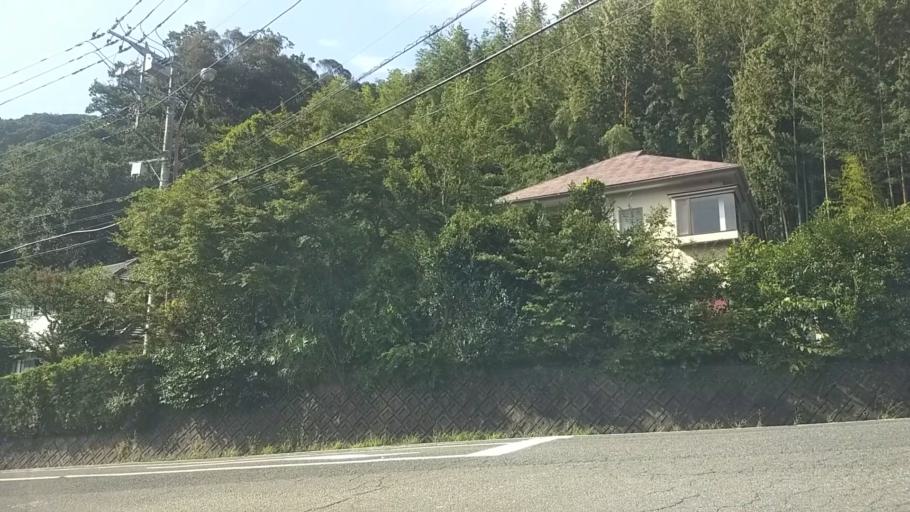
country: JP
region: Shizuoka
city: Heda
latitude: 34.9708
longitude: 138.9181
